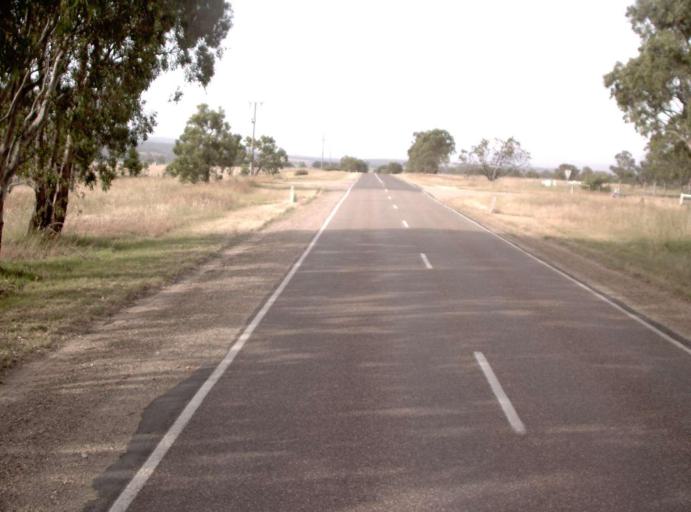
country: AU
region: Victoria
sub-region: Wellington
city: Heyfield
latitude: -38.0275
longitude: 146.6685
